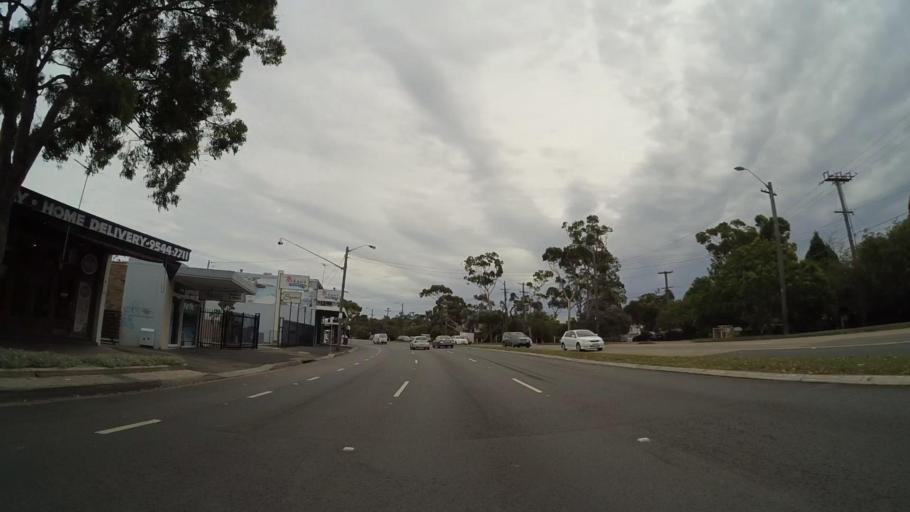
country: AU
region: New South Wales
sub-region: Sutherland Shire
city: Kareela
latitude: -34.0116
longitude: 151.0945
